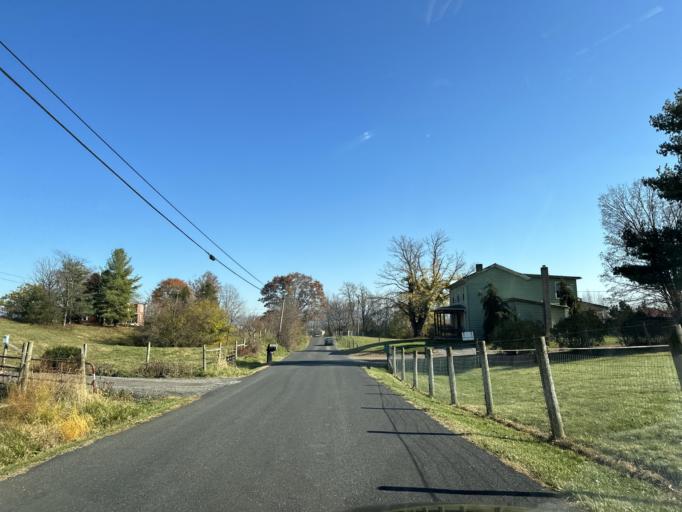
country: US
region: Virginia
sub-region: Augusta County
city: Weyers Cave
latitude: 38.2925
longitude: -78.9197
